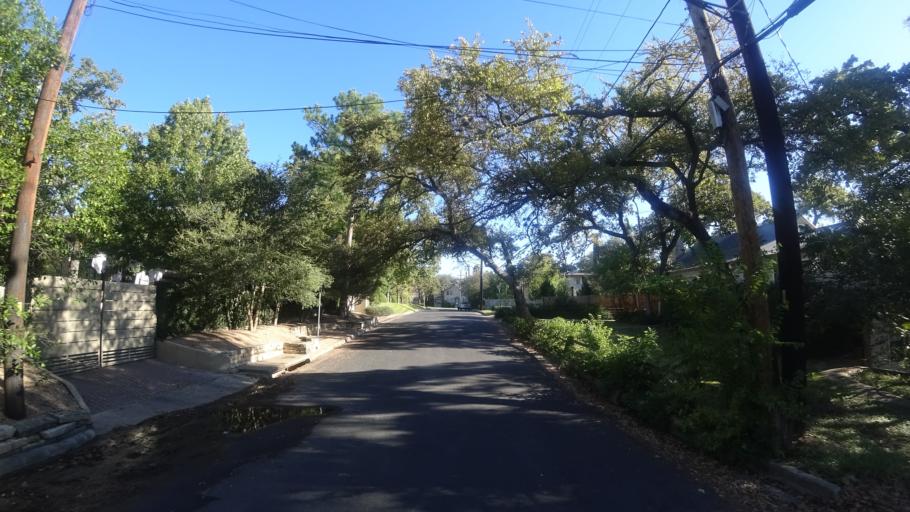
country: US
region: Texas
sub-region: Travis County
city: Rollingwood
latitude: 30.2863
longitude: -97.7668
